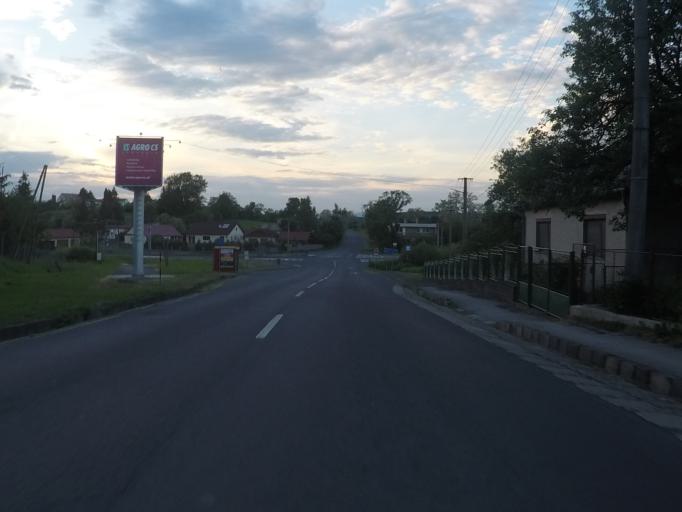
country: SK
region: Banskobystricky
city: Poltar
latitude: 48.3615
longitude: 19.8307
